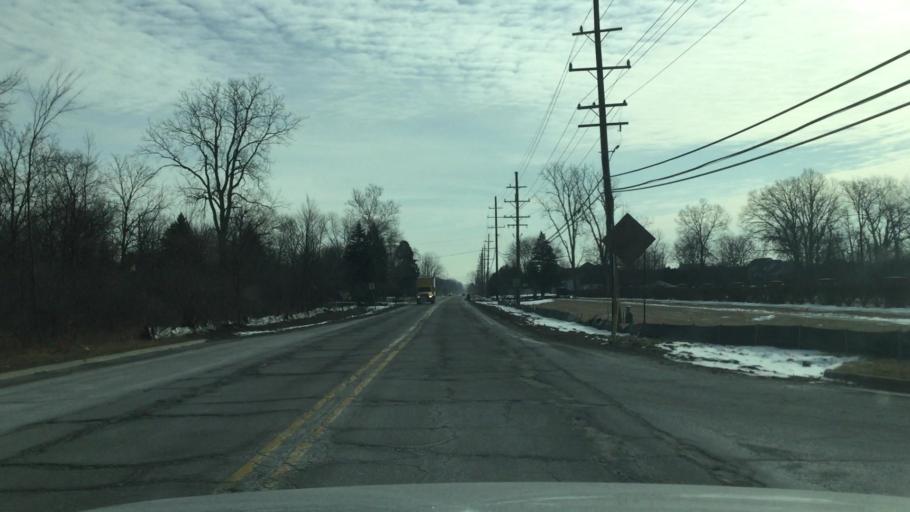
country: US
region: Michigan
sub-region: Wayne County
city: Flat Rock
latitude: 42.1234
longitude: -83.2965
